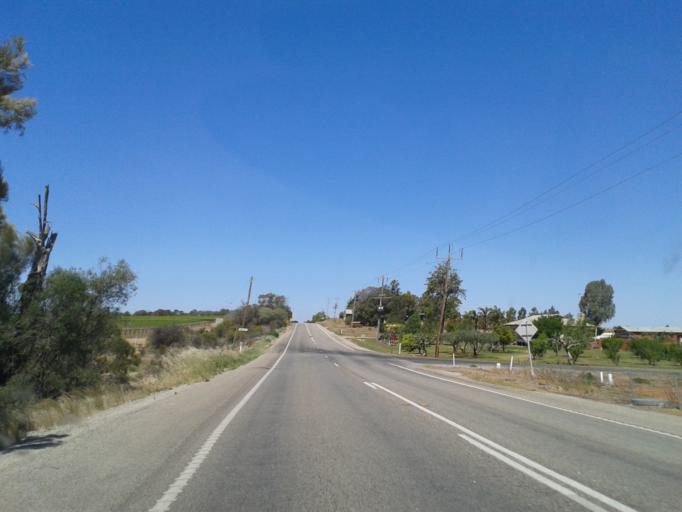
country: AU
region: Victoria
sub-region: Mildura Shire
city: Ouyen
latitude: -34.6180
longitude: 142.8019
